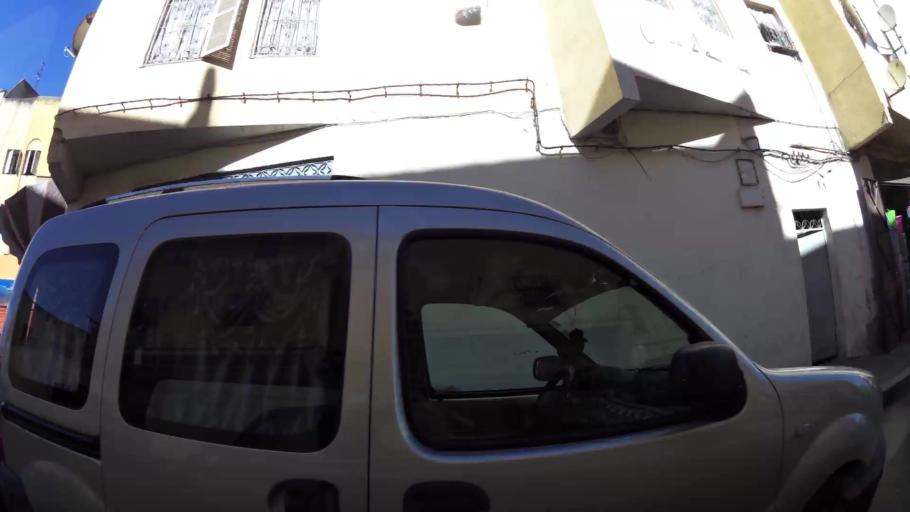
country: MA
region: Fes-Boulemane
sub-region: Fes
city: Fes
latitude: 34.0632
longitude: -4.9644
